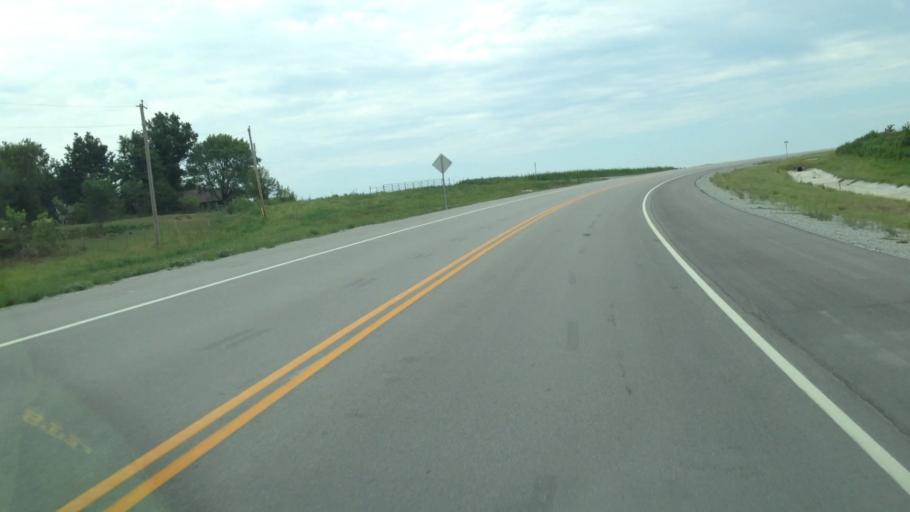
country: US
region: Kansas
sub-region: Labette County
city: Chetopa
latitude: 36.8870
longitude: -95.0986
